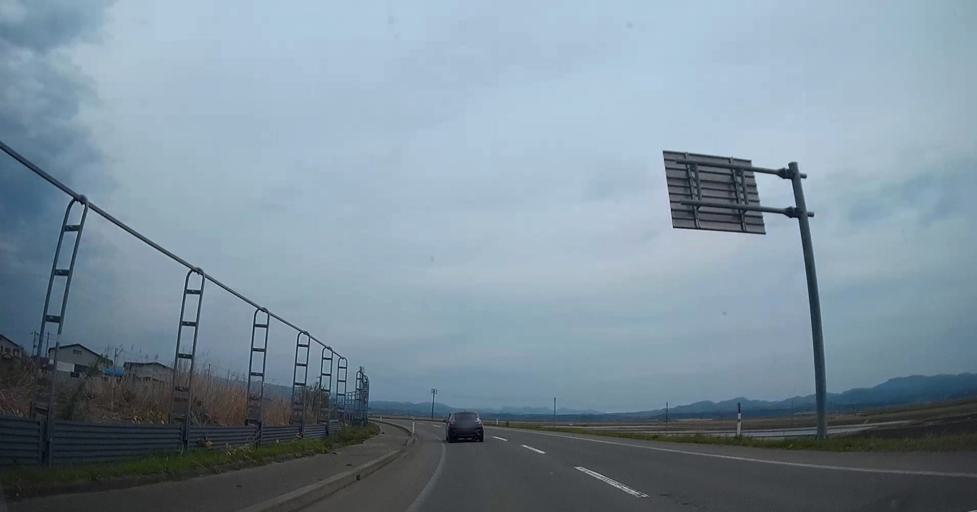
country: JP
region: Aomori
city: Shimokizukuri
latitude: 40.9791
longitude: 140.3756
